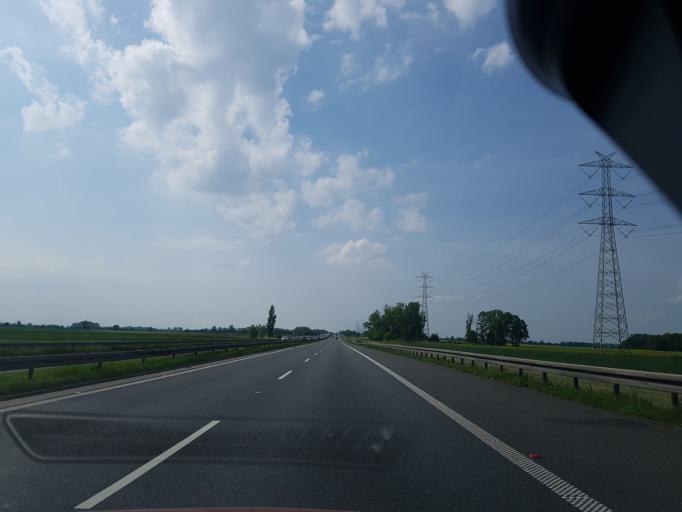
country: PL
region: Lower Silesian Voivodeship
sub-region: Powiat olawski
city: Wierzbno
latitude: 50.8977
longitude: 17.1765
